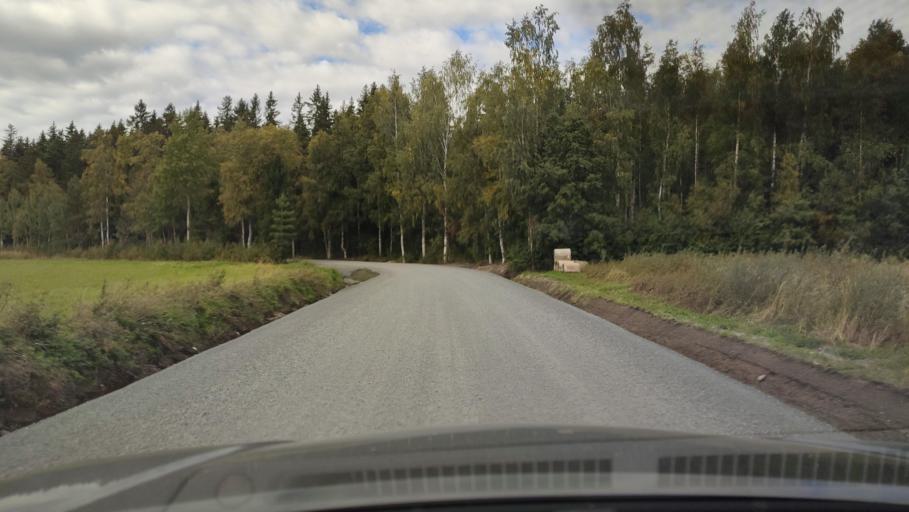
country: FI
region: Southern Ostrobothnia
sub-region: Suupohja
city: Karijoki
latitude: 62.2322
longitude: 21.6149
